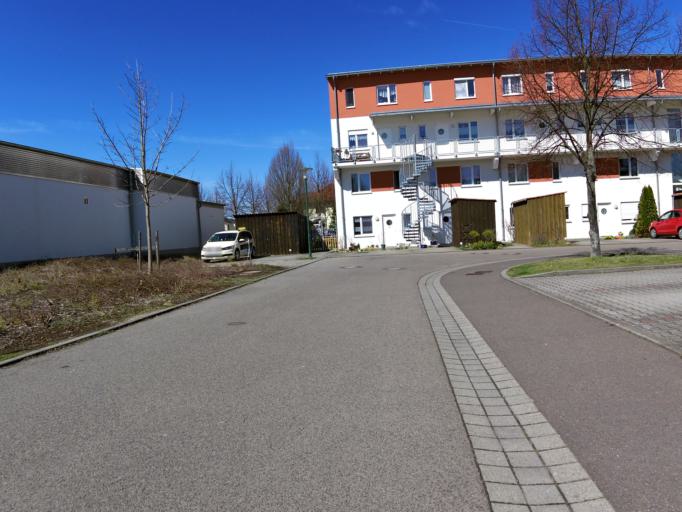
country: DE
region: Saxony
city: Taucha
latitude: 51.3597
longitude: 12.4745
